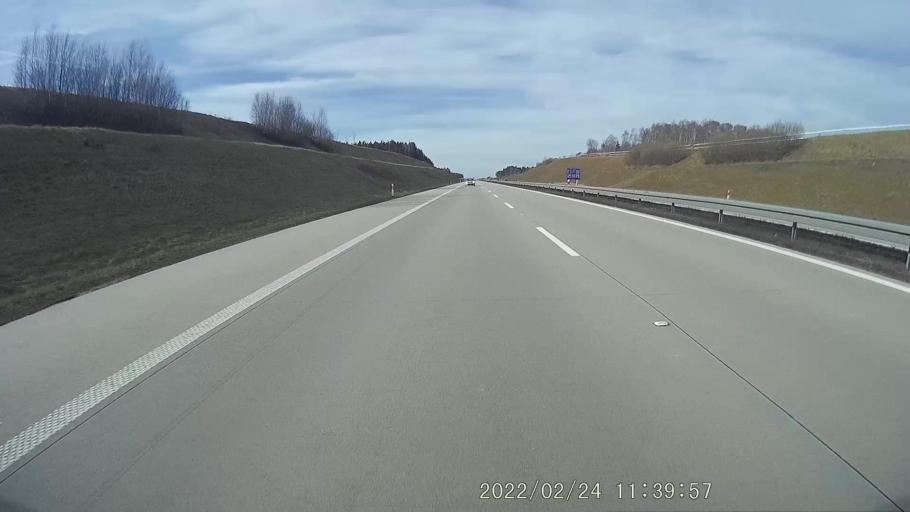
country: PL
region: Lower Silesian Voivodeship
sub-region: Powiat polkowicki
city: Przemkow
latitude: 51.5375
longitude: 15.8674
